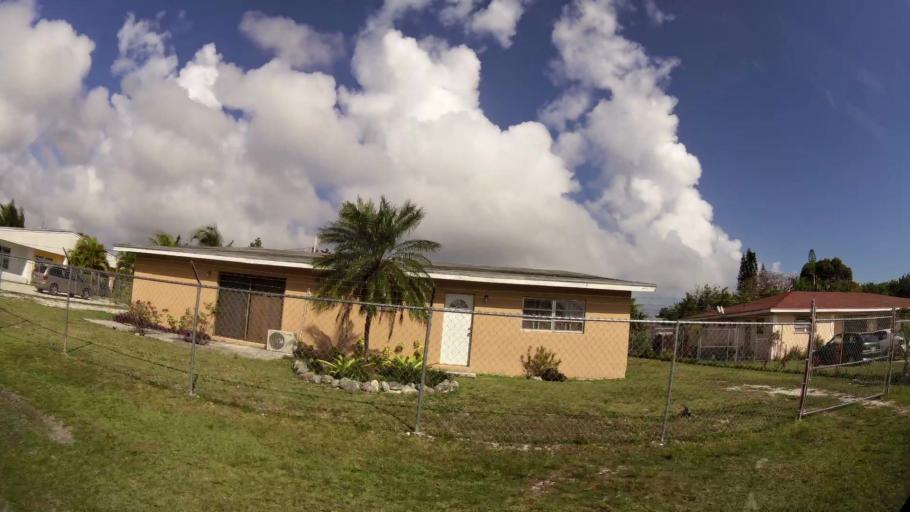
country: BS
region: Freeport
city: Freeport
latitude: 26.5195
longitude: -78.6904
